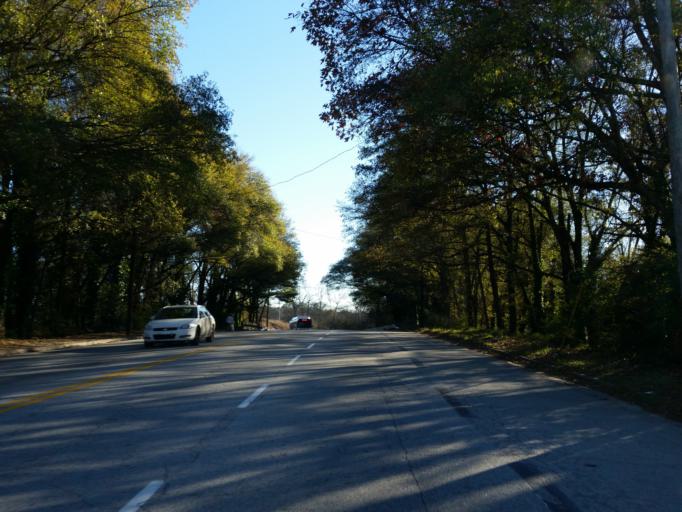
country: US
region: Georgia
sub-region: Fulton County
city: Atlanta
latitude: 33.7755
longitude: -84.4261
